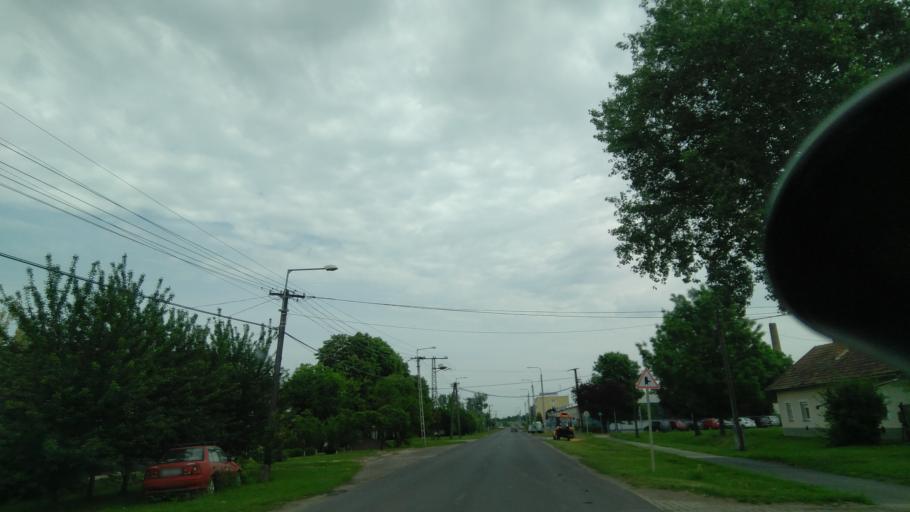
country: HU
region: Bekes
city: Szeghalom
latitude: 47.0294
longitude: 21.1697
